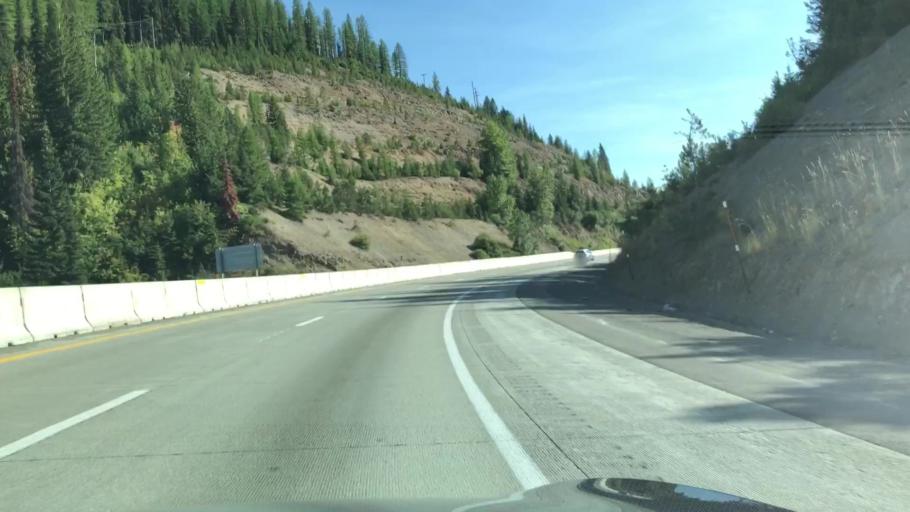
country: US
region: Idaho
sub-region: Shoshone County
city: Wallace
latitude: 47.4607
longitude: -115.6941
